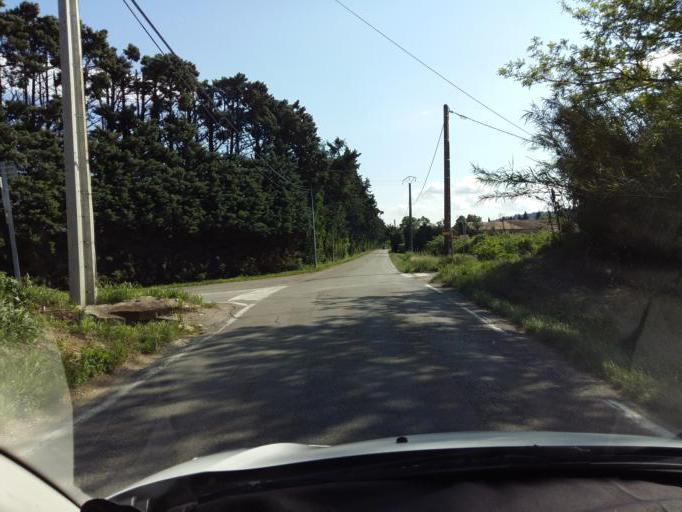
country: FR
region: Provence-Alpes-Cote d'Azur
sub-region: Departement du Vaucluse
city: Cavaillon
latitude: 43.8549
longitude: 5.0529
